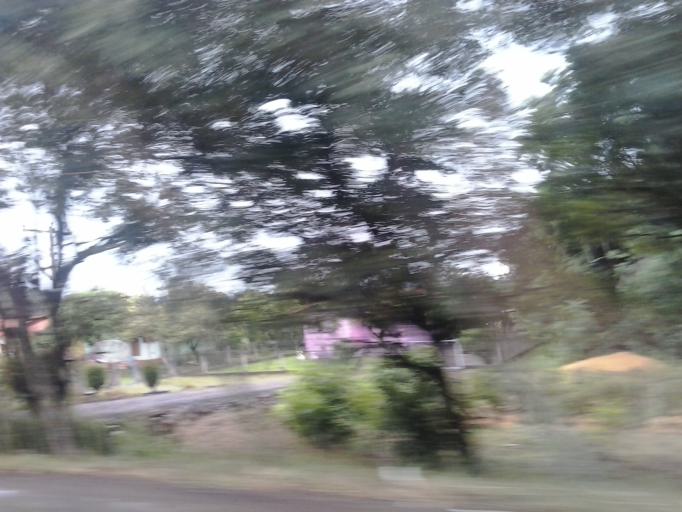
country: BR
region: Rio Grande do Sul
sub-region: Candelaria
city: Candelaria
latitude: -29.7173
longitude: -53.2398
